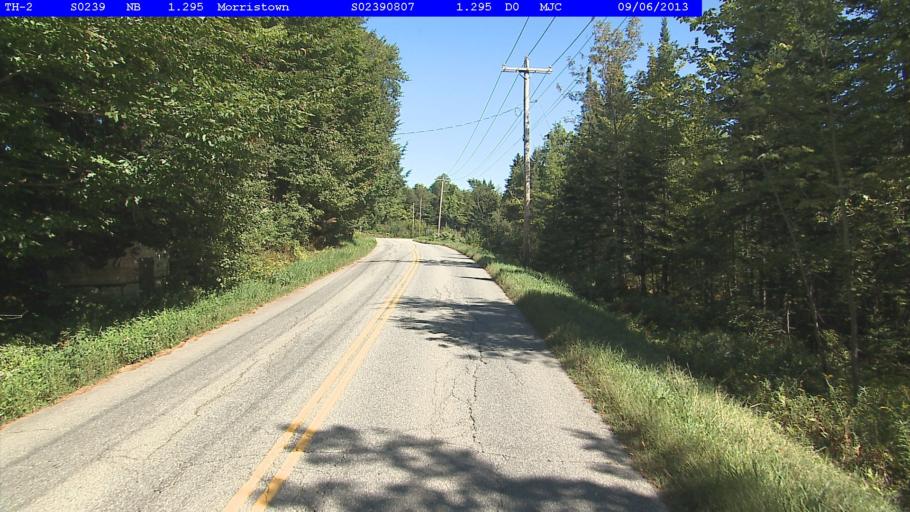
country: US
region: Vermont
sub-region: Lamoille County
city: Morristown
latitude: 44.5727
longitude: -72.6139
